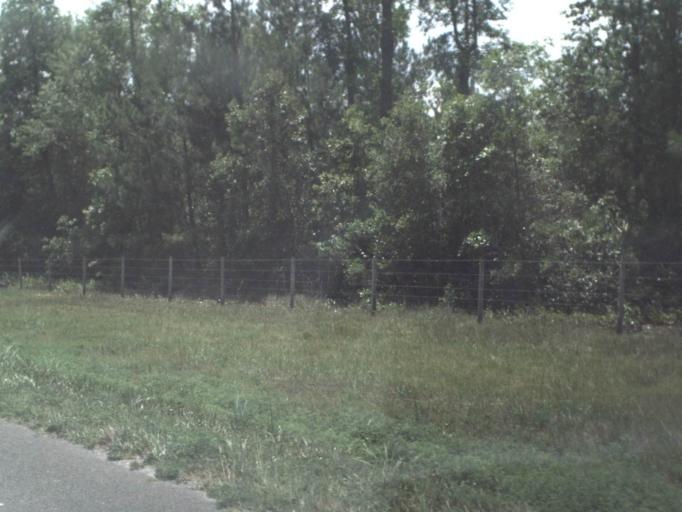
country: US
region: Florida
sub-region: Nassau County
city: Nassau Village-Ratliff
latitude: 30.4956
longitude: -81.7412
